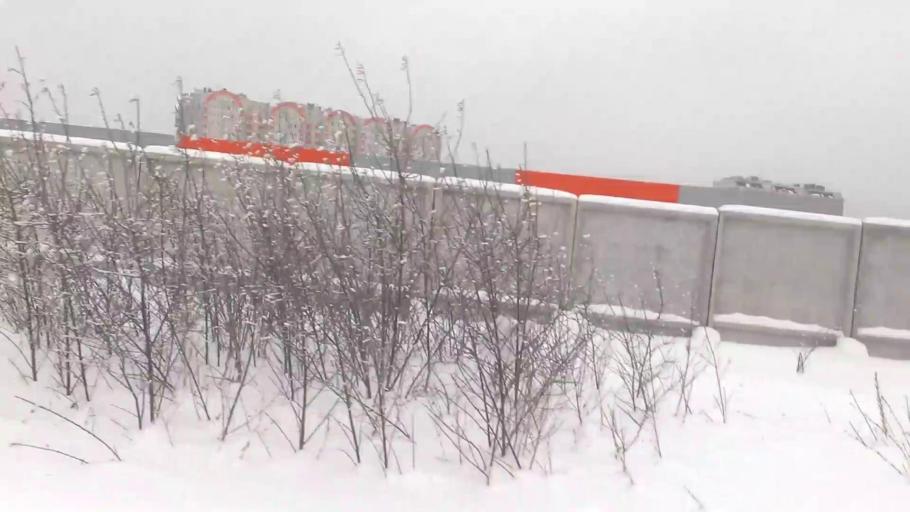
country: RU
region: Altai Krai
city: Novosilikatnyy
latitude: 53.3518
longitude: 83.6604
